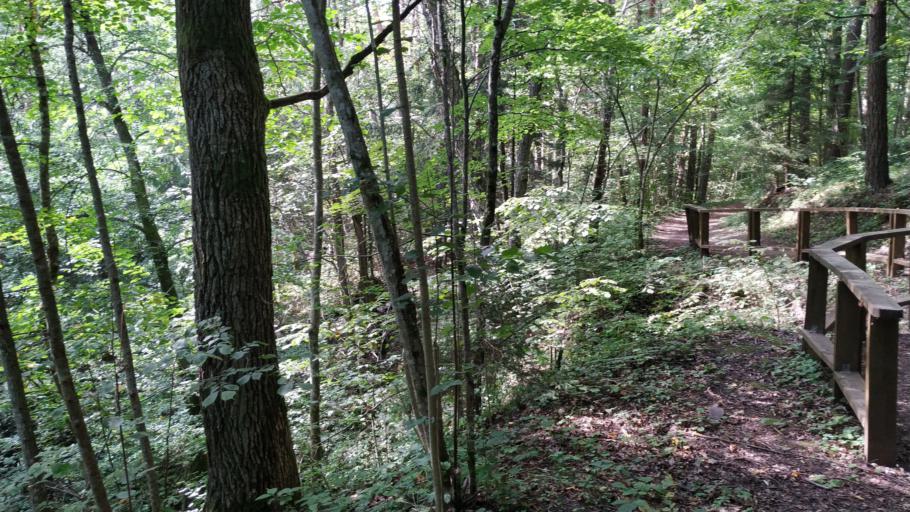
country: LT
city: Grigiskes
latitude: 54.8088
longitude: 24.9727
